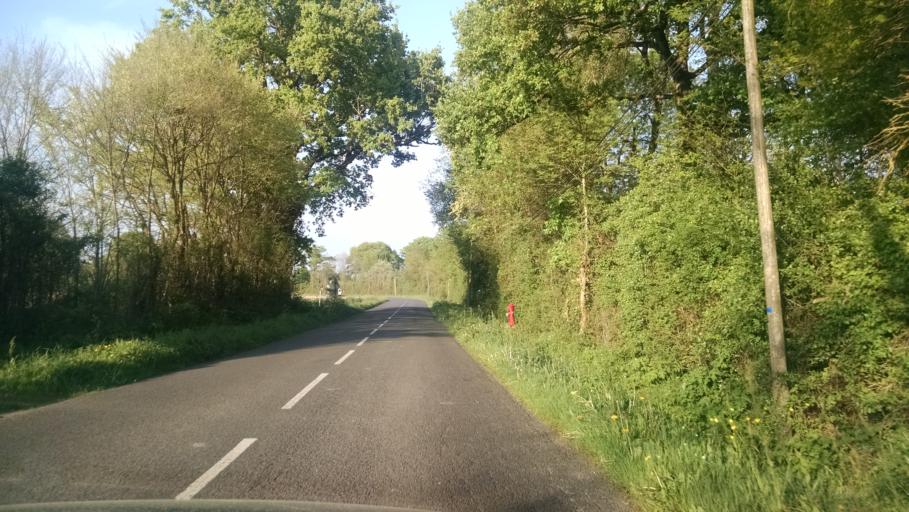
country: FR
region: Pays de la Loire
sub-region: Departement de la Loire-Atlantique
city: Saint-Lumine-de-Clisson
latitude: 47.0690
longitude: -1.3505
